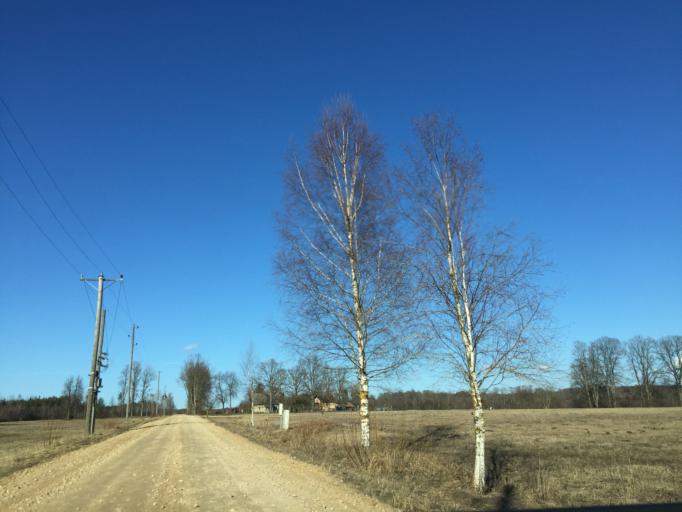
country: LV
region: Ogre
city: Ogre
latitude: 56.8665
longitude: 24.7046
